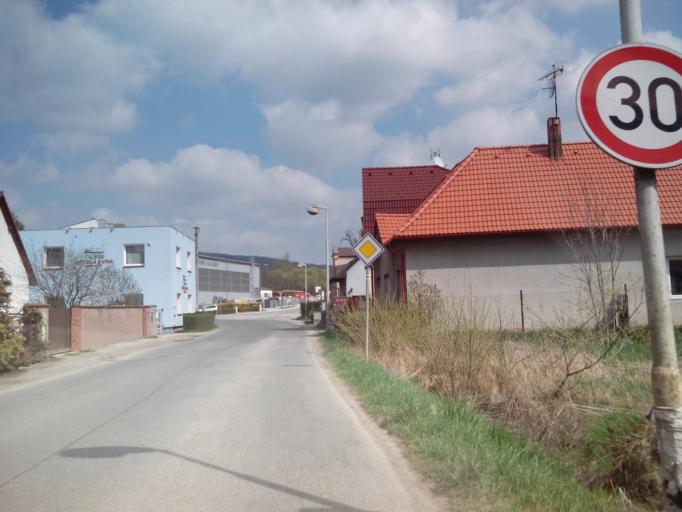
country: CZ
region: Central Bohemia
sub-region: Okres Beroun
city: Lodenice
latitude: 49.9915
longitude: 14.1604
